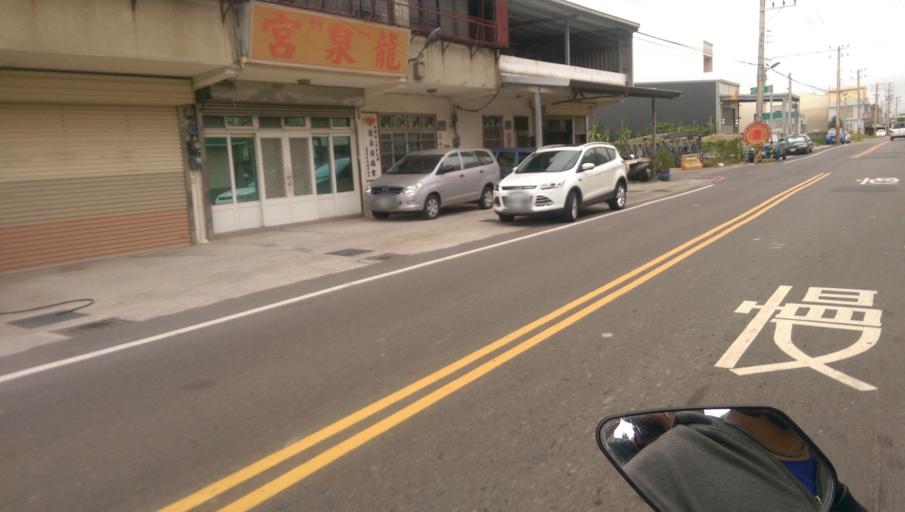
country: TW
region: Taiwan
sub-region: Hsinchu
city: Hsinchu
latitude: 24.8155
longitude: 120.9289
